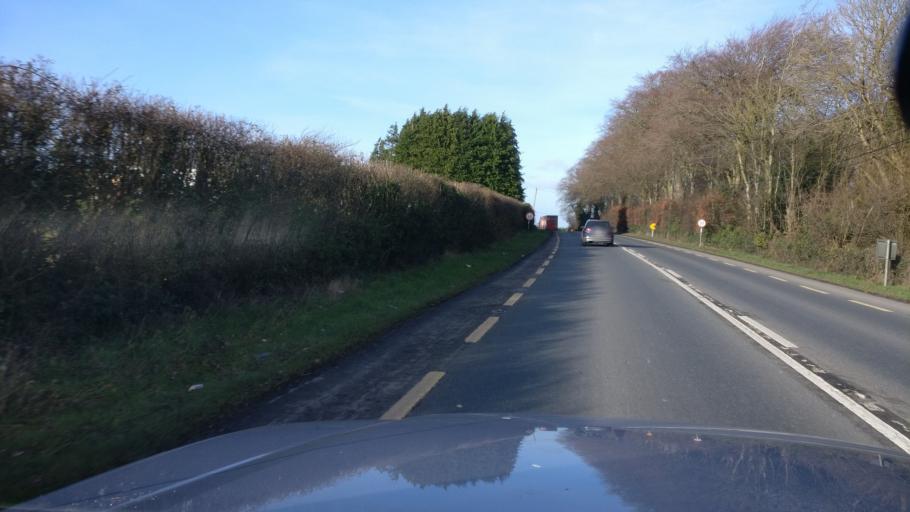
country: IE
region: Leinster
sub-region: Uibh Fhaili
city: Tullamore
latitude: 53.2511
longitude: -7.4772
